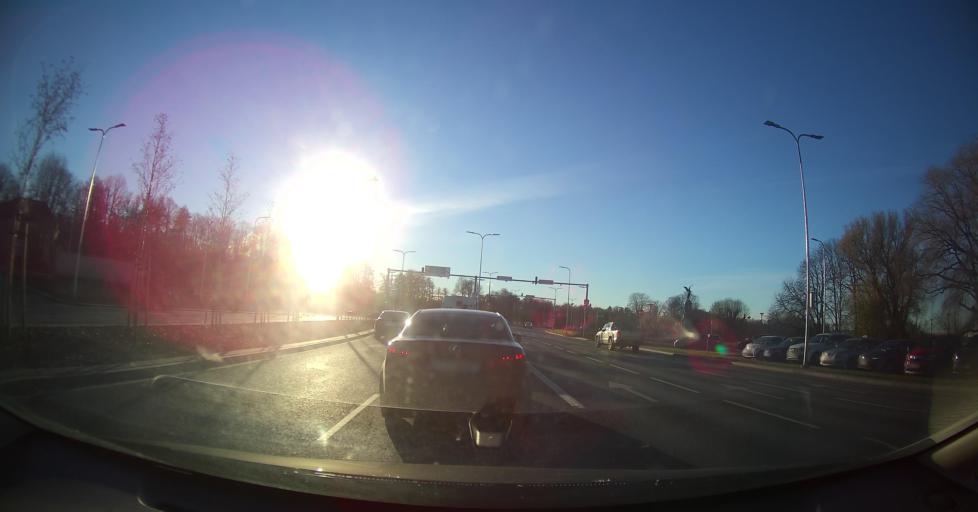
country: EE
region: Harju
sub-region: Tallinna linn
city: Tallinn
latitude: 59.4441
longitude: 24.7976
